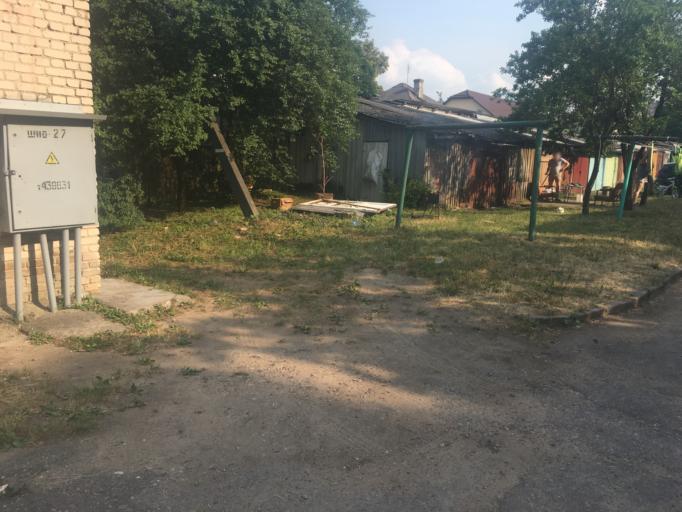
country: BY
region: Grodnenskaya
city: Hrodna
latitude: 53.6654
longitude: 23.8015
